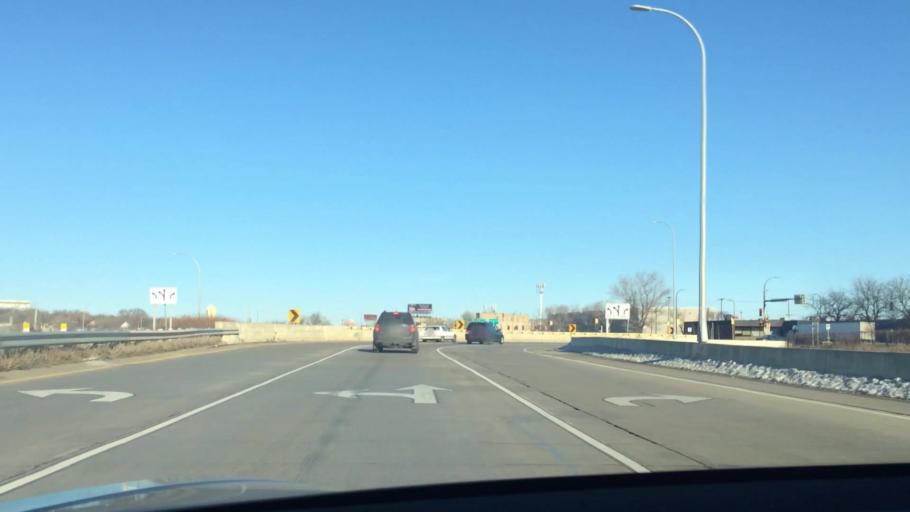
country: US
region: Minnesota
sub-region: Hennepin County
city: Minneapolis
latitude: 44.9955
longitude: -93.2827
